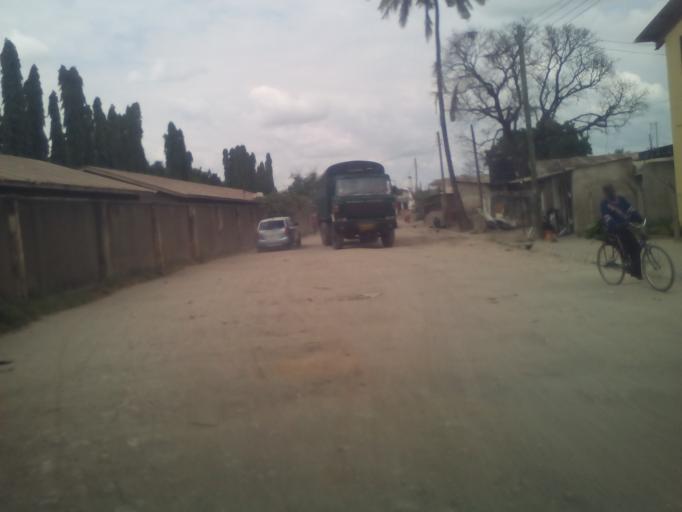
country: TZ
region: Dar es Salaam
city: Dar es Salaam
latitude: -6.8561
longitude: 39.2444
